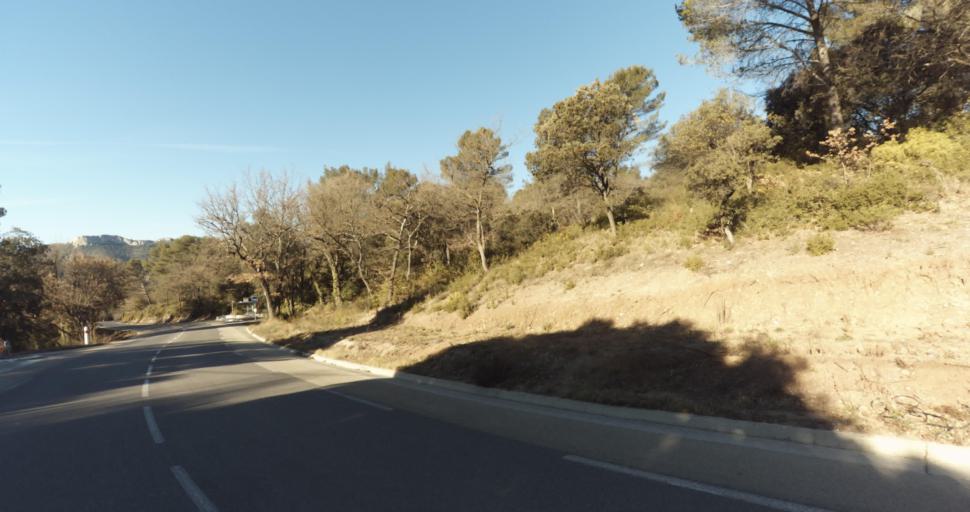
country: FR
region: Provence-Alpes-Cote d'Azur
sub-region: Departement des Bouches-du-Rhone
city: Peypin
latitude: 43.4054
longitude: 5.5733
